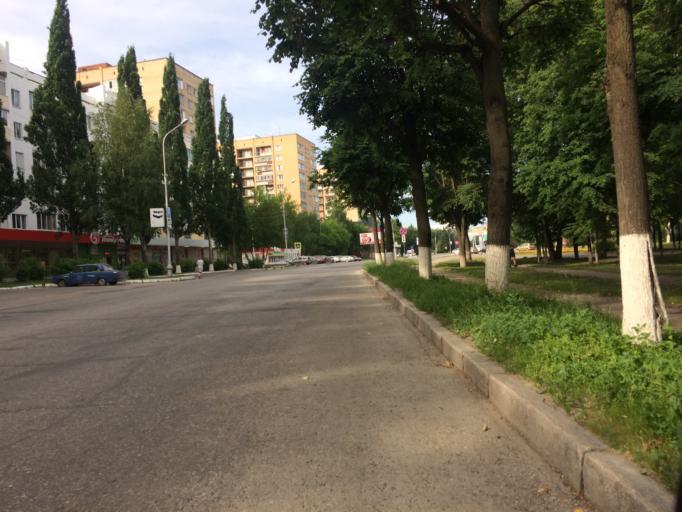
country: RU
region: Mariy-El
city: Yoshkar-Ola
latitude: 56.6261
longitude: 47.8906
